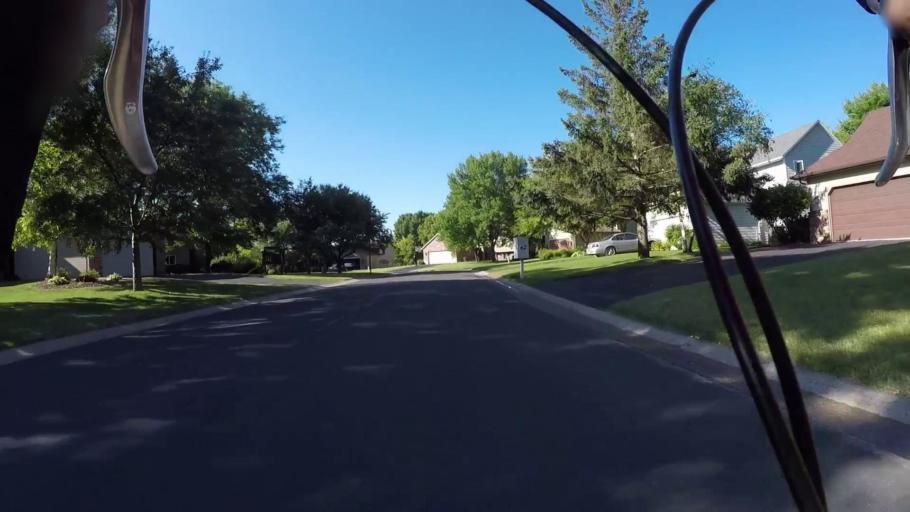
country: US
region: Minnesota
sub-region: Carver County
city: Chanhassen
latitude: 44.8745
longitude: -93.5052
